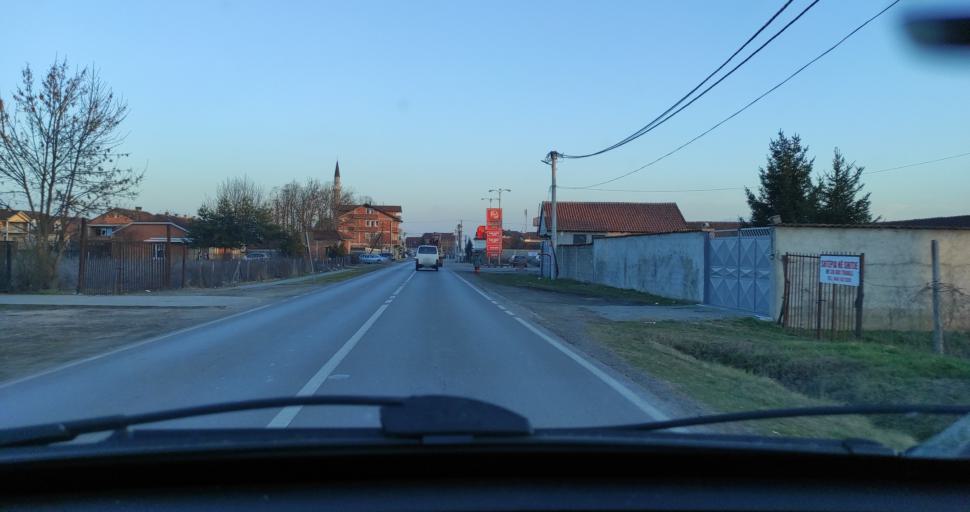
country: XK
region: Gjakova
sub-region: Komuna e Gjakoves
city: Gjakove
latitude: 42.4320
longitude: 20.3810
